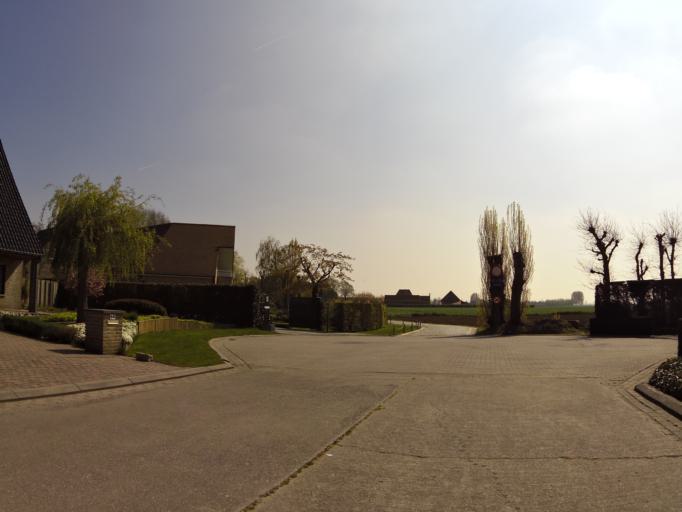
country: BE
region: Flanders
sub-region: Provincie West-Vlaanderen
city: Gistel
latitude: 51.1504
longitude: 2.9421
